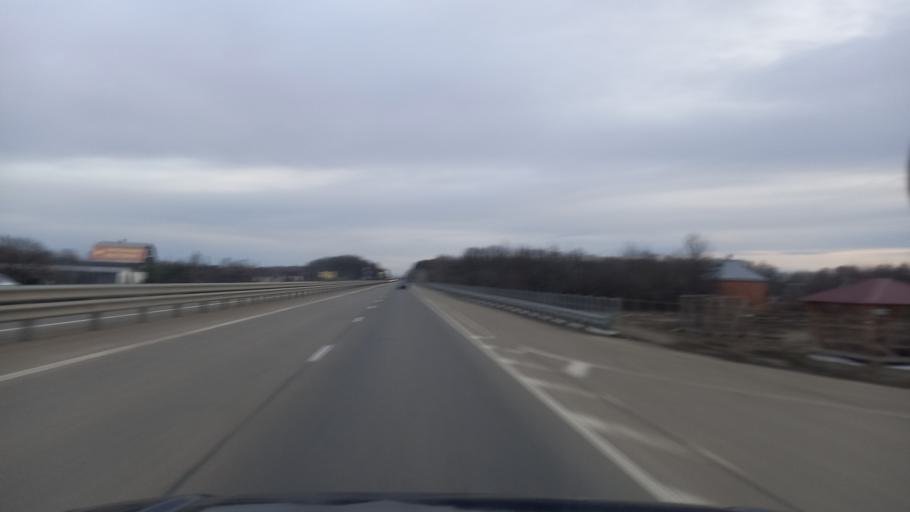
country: RU
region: Adygeya
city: Khanskaya
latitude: 44.7260
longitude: 39.9495
